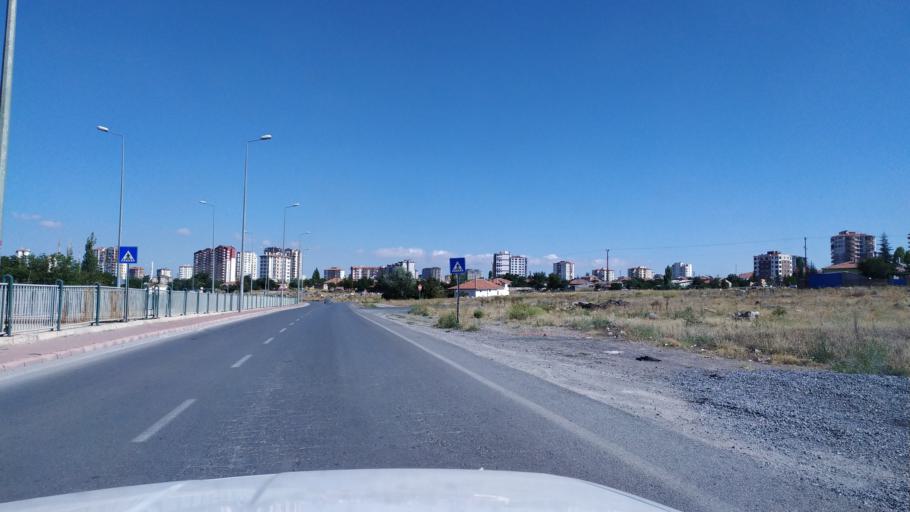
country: TR
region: Kayseri
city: Talas
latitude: 38.7311
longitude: 35.5493
